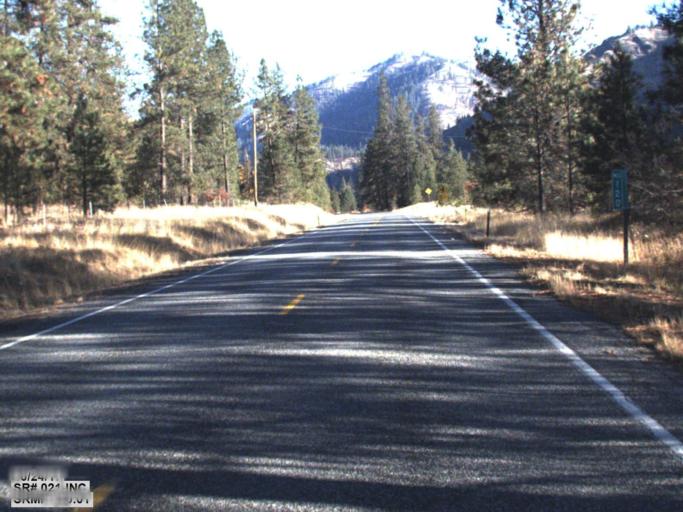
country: US
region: Washington
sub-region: Okanogan County
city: Coulee Dam
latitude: 48.1217
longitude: -118.6943
